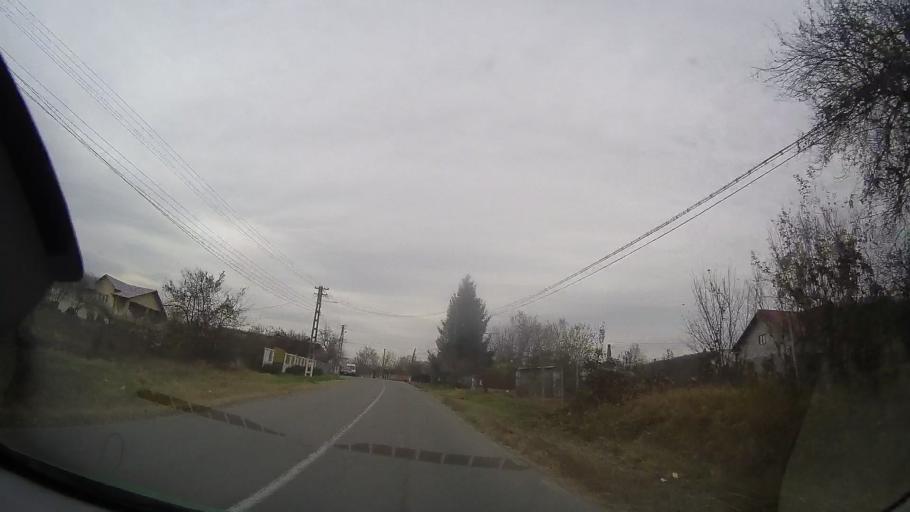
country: RO
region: Prahova
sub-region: Comuna Iordachianu
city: Iordacheanu
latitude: 45.0279
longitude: 26.2392
